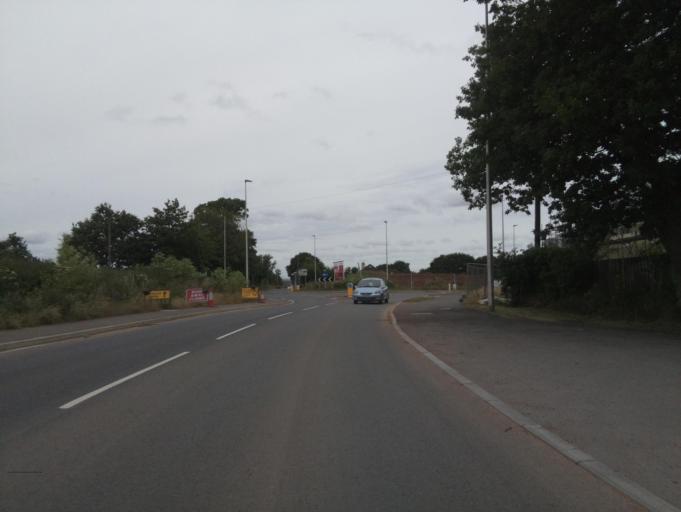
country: GB
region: England
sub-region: Devon
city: Bradninch
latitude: 50.7510
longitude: -3.3872
